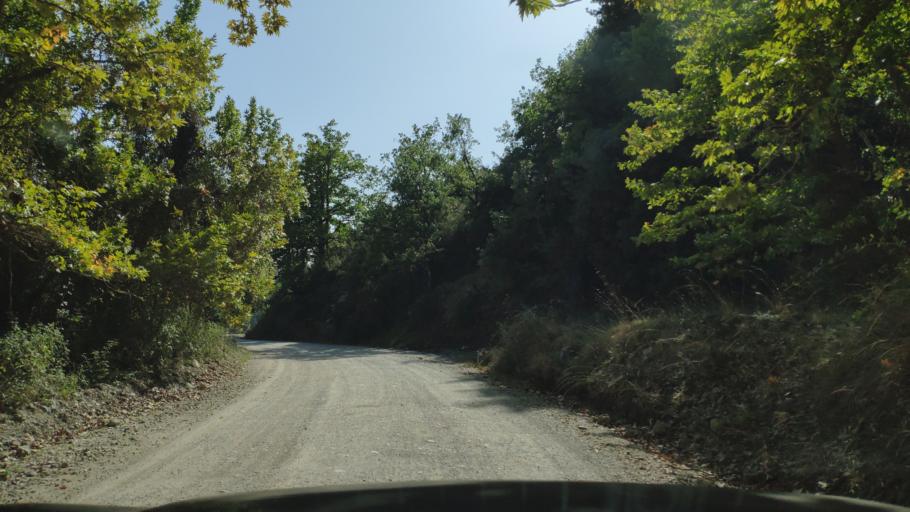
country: GR
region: West Greece
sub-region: Nomos Achaias
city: Aiyira
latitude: 37.9422
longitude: 22.3174
